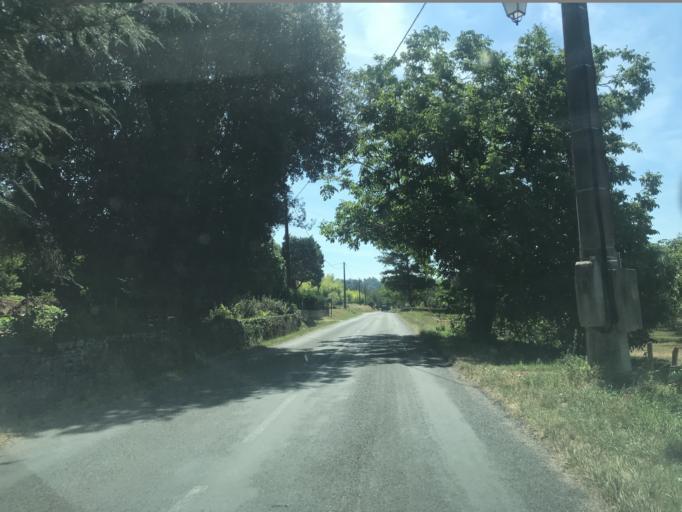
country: FR
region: Aquitaine
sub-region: Departement de la Dordogne
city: Cenac-et-Saint-Julien
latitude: 44.8188
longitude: 1.1912
